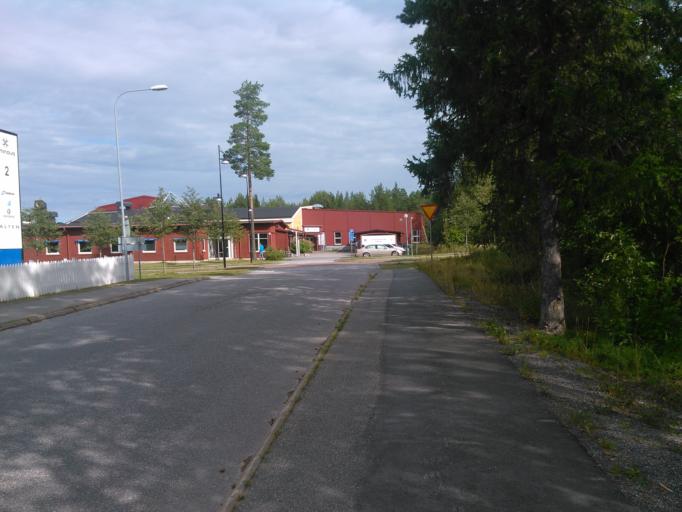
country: SE
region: Vaesterbotten
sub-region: Umea Kommun
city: Umea
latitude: 63.8176
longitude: 20.3211
